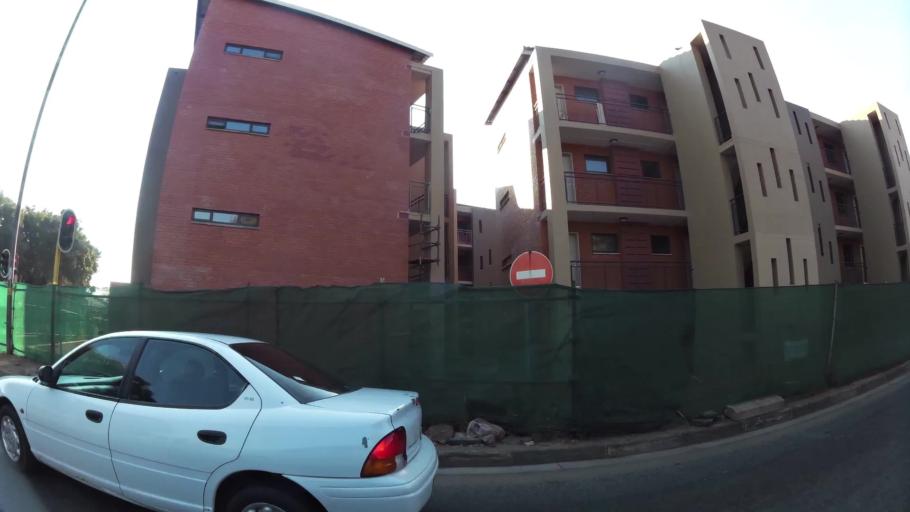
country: ZA
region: Gauteng
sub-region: Ekurhuleni Metropolitan Municipality
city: Germiston
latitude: -26.2202
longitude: 28.1692
